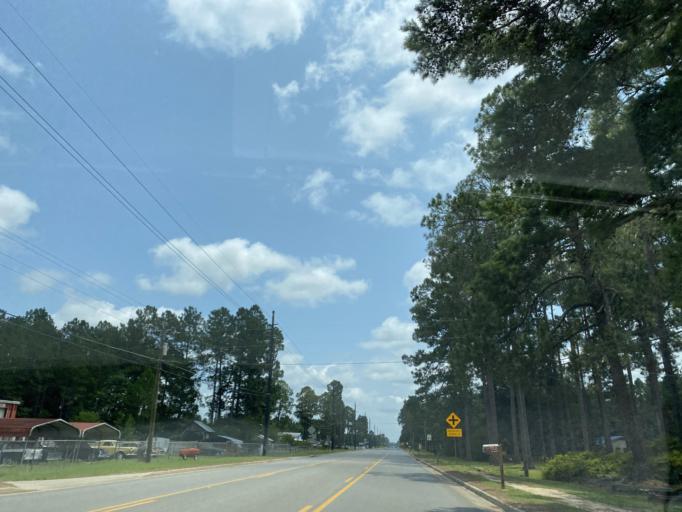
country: US
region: Georgia
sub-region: Jeff Davis County
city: Hazlehurst
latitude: 31.8442
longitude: -82.5860
